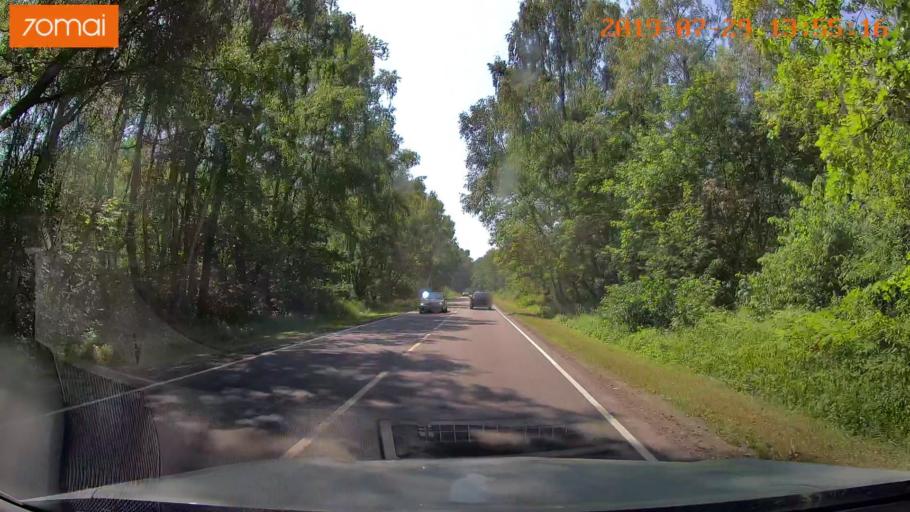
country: RU
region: Kaliningrad
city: Primorsk
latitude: 54.7167
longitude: 19.9587
